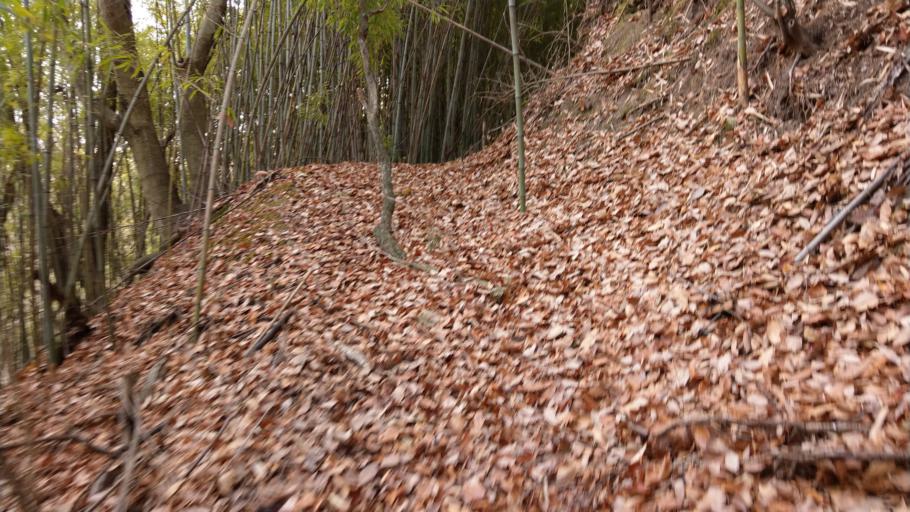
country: JP
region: Nagano
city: Komoro
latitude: 36.3222
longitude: 138.4202
